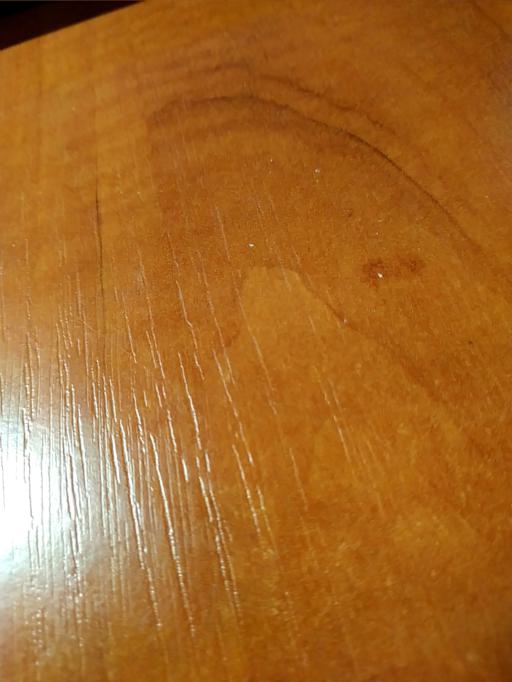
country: RU
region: Tverskaya
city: Zubtsov
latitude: 56.1571
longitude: 34.6481
